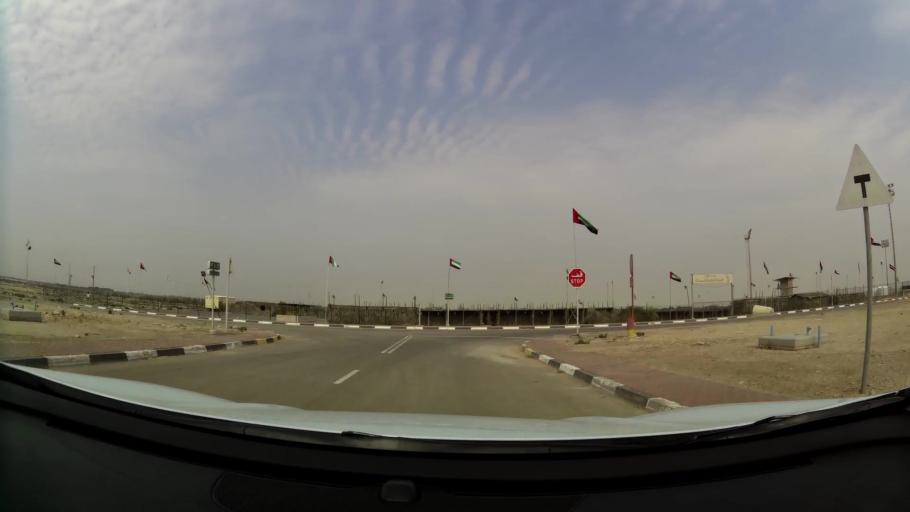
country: AE
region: Abu Dhabi
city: Abu Dhabi
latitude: 24.6858
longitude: 54.7653
